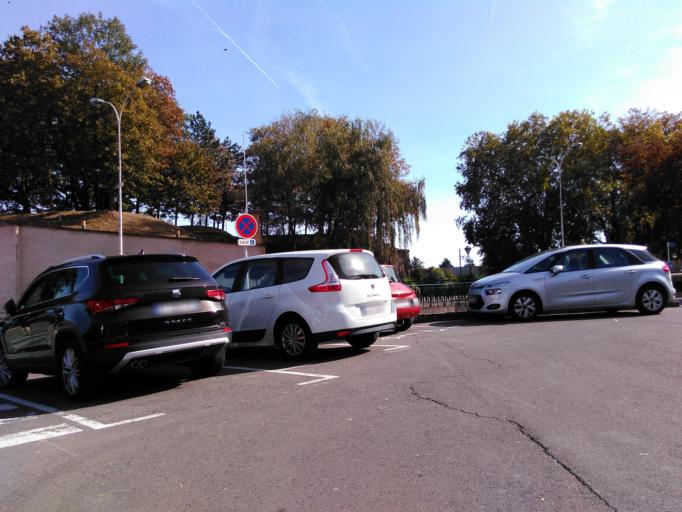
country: FR
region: Lorraine
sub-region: Departement de la Moselle
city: Thionville
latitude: 49.3588
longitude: 6.1700
